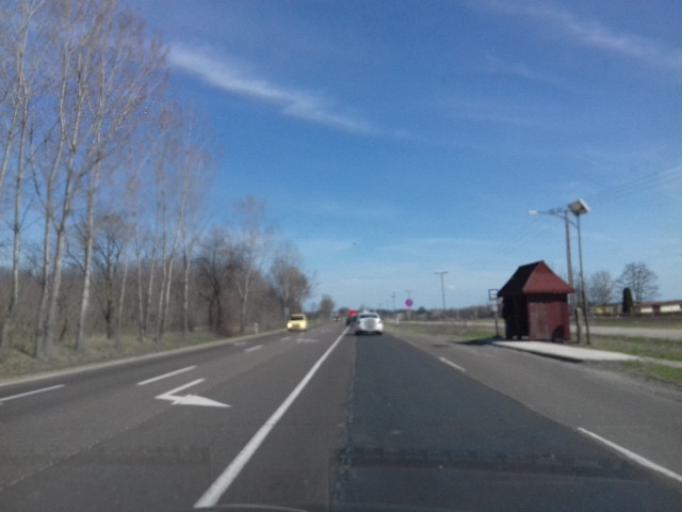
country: HU
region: Bacs-Kiskun
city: Nyarlorinc
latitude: 46.8675
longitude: 19.8805
